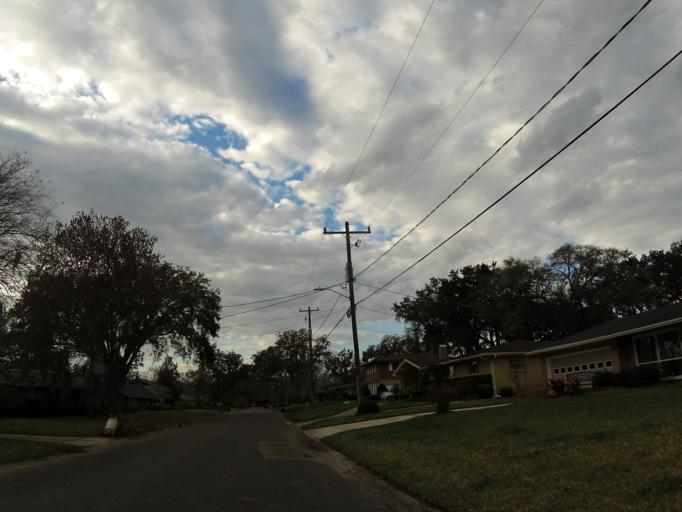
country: US
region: Florida
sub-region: Duval County
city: Jacksonville
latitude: 30.2511
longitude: -81.6372
